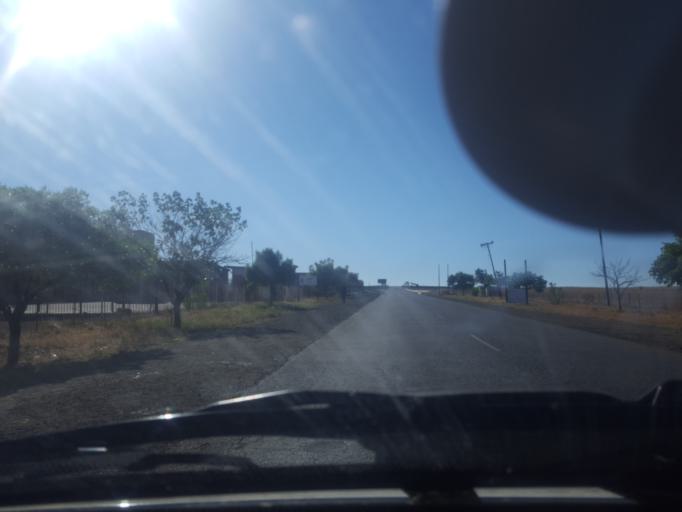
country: ZA
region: Orange Free State
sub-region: Xhariep District Municipality
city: Trompsburg
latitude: -30.0342
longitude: 25.7876
